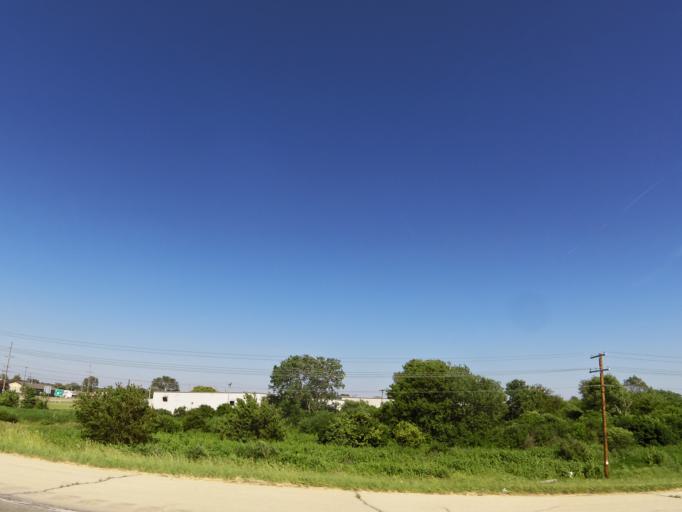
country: US
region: Illinois
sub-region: Winnebago County
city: South Beloit
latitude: 42.4553
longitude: -89.0193
